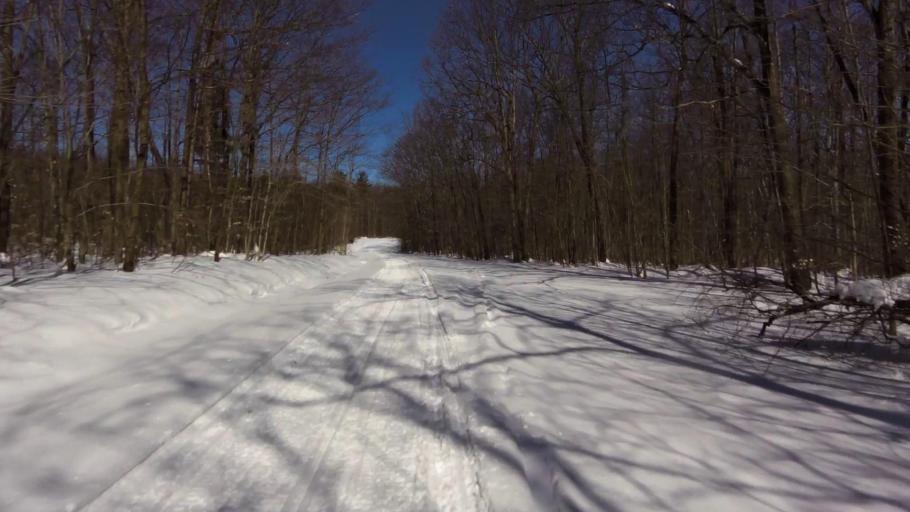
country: US
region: New York
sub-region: Allegany County
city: Cuba
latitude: 42.3222
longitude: -78.2326
